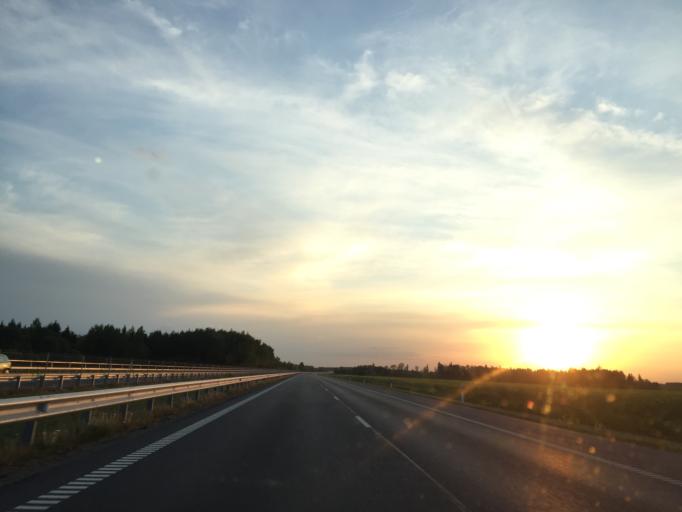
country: LT
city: Kursenai
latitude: 55.9843
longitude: 23.1002
